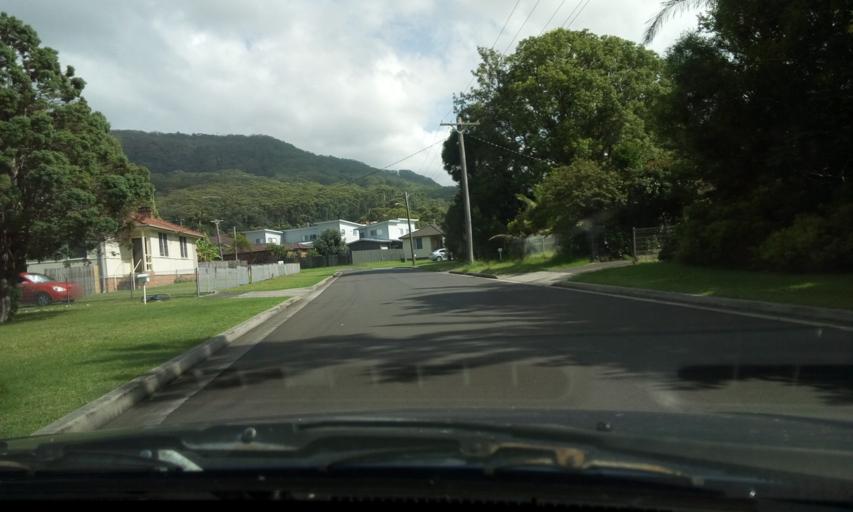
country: AU
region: New South Wales
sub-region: Wollongong
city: Corrimal
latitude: -34.3762
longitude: 150.8904
